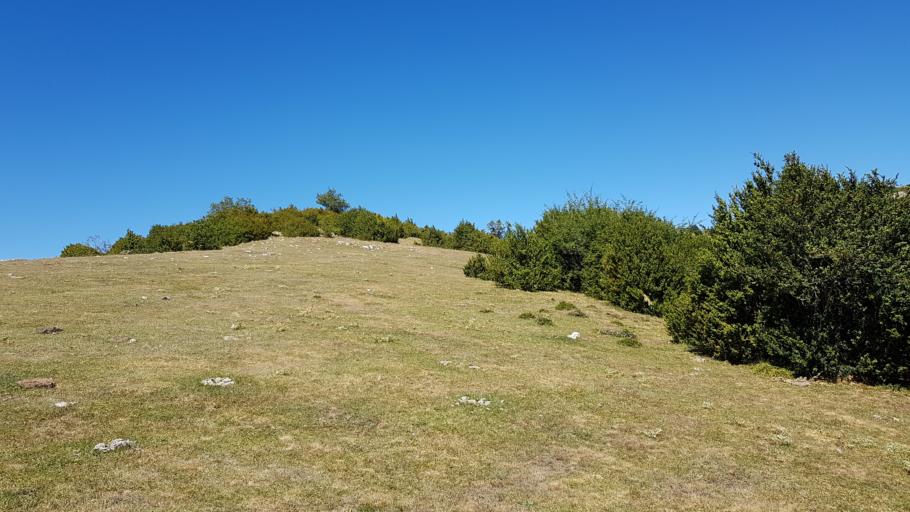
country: ES
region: La Rioja
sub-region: Provincia de La Rioja
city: Nestares
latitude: 42.2833
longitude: -2.6509
